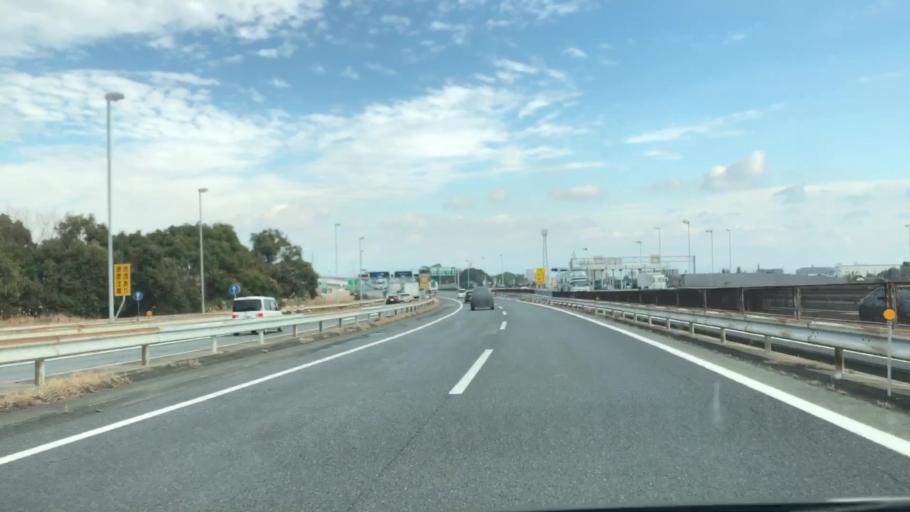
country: JP
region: Saga Prefecture
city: Tosu
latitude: 33.3940
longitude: 130.5295
